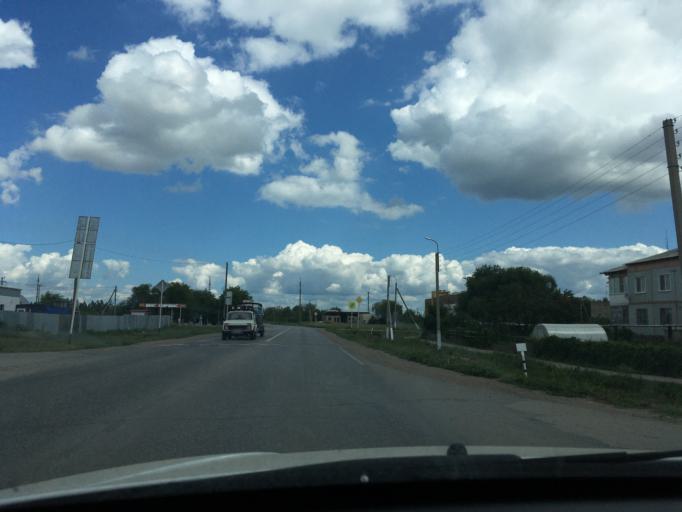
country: RU
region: Samara
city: Bezenchuk
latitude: 52.9947
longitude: 49.4381
